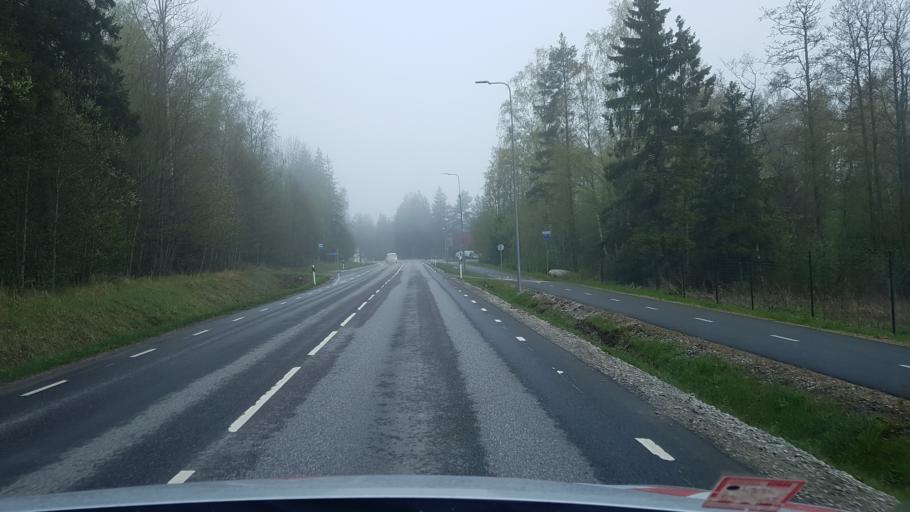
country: EE
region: Harju
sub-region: Viimsi vald
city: Viimsi
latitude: 59.5287
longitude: 24.8783
